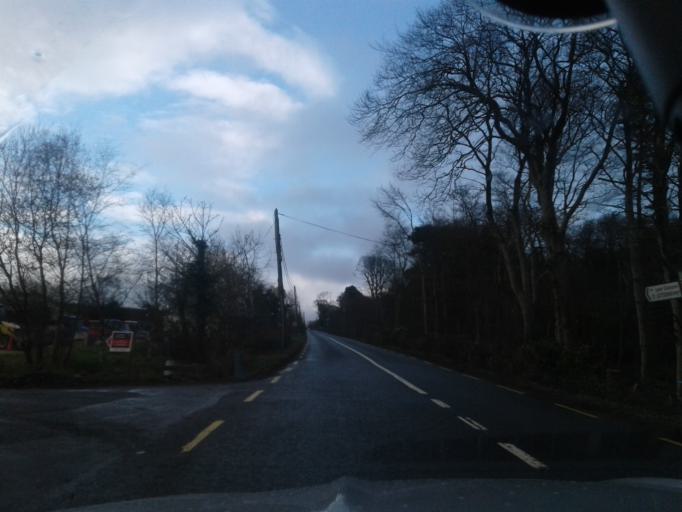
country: IE
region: Ulster
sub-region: County Donegal
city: Ramelton
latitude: 55.0187
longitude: -7.6531
